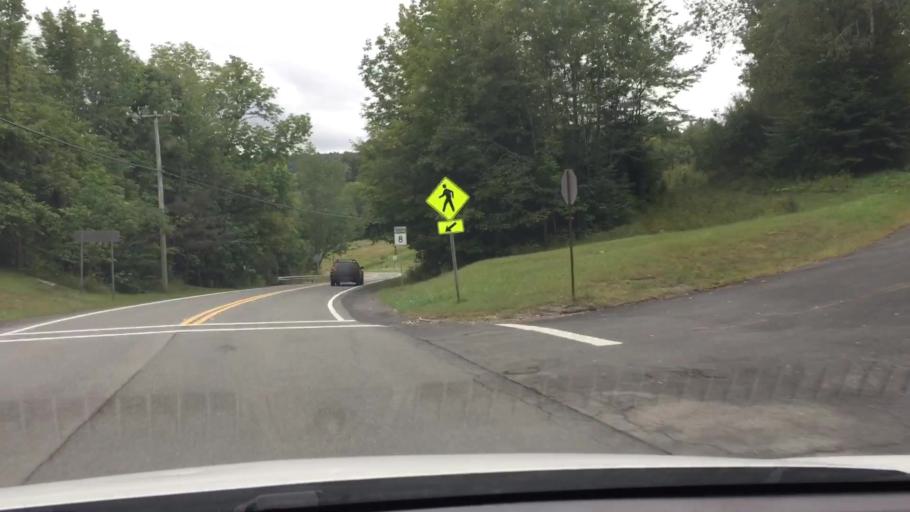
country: US
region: Massachusetts
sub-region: Berkshire County
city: Becket
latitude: 42.3733
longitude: -73.1163
